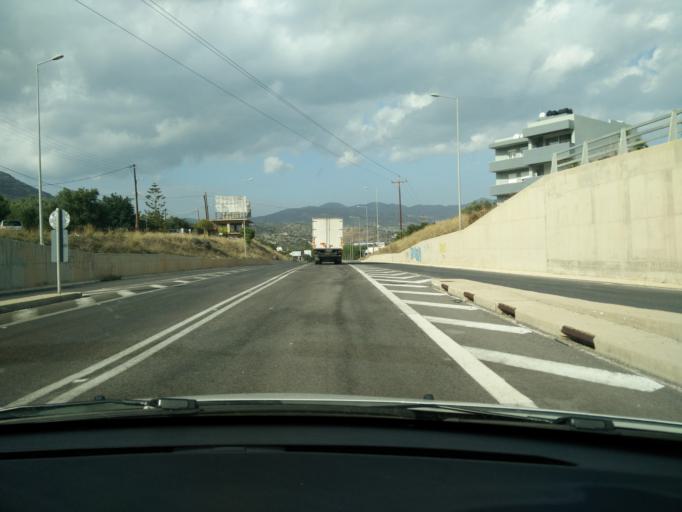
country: GR
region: Crete
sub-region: Nomos Lasithiou
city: Agios Nikolaos
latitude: 35.1867
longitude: 25.7043
